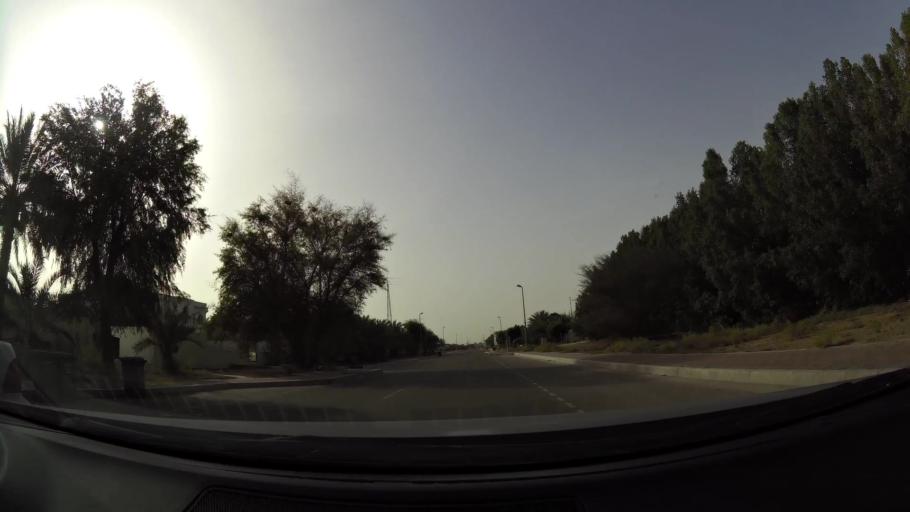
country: AE
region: Abu Dhabi
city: Al Ain
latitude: 24.2159
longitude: 55.6582
